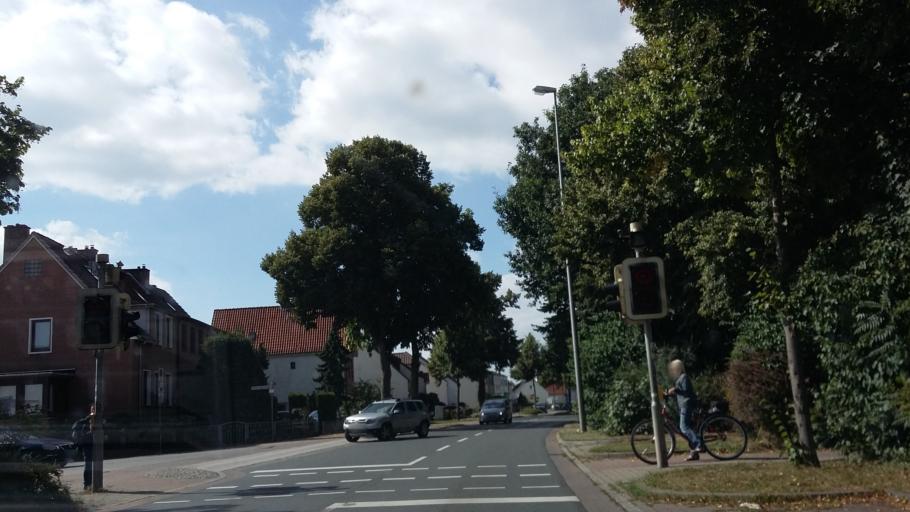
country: DE
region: Bremen
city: Bremen
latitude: 53.0440
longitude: 8.8240
